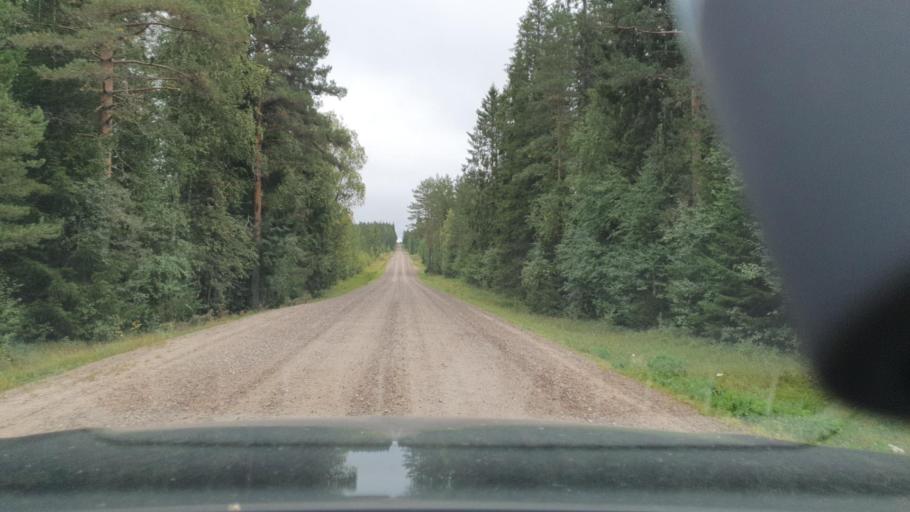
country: SE
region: Vaermland
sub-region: Torsby Kommun
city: Torsby
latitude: 60.4916
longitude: 12.9404
